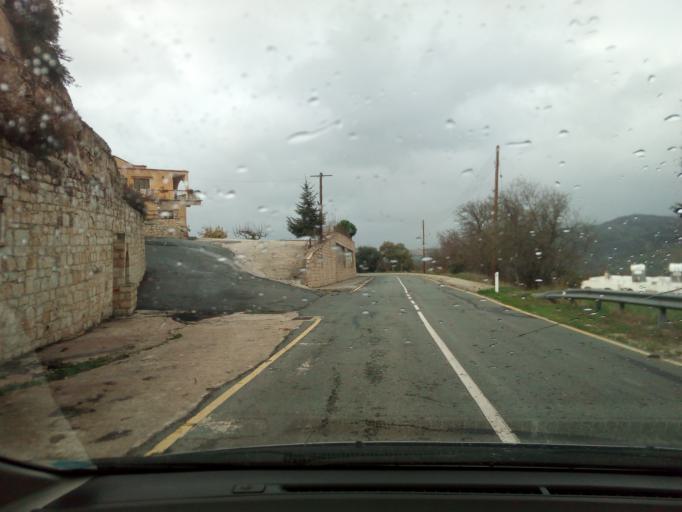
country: CY
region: Pafos
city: Polis
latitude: 34.9406
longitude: 32.5078
